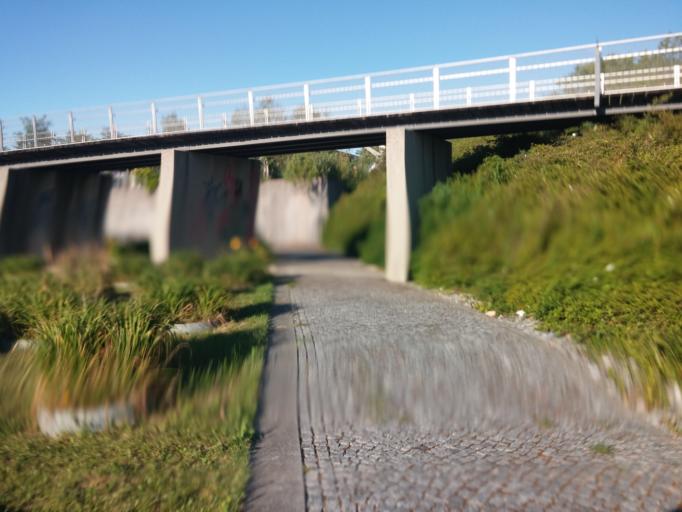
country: DE
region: Bavaria
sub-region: Upper Bavaria
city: Haar
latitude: 48.1279
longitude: 11.6872
